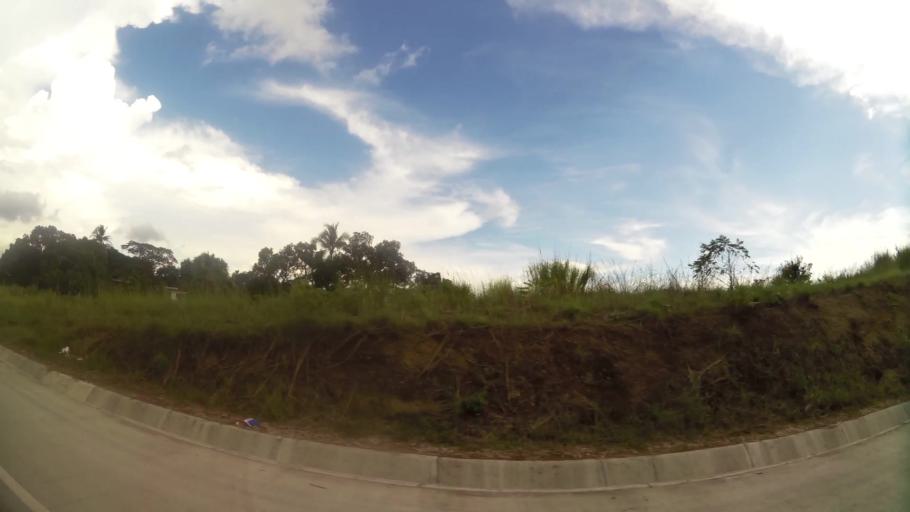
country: PA
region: Panama
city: Tocumen
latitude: 9.1001
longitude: -79.4174
